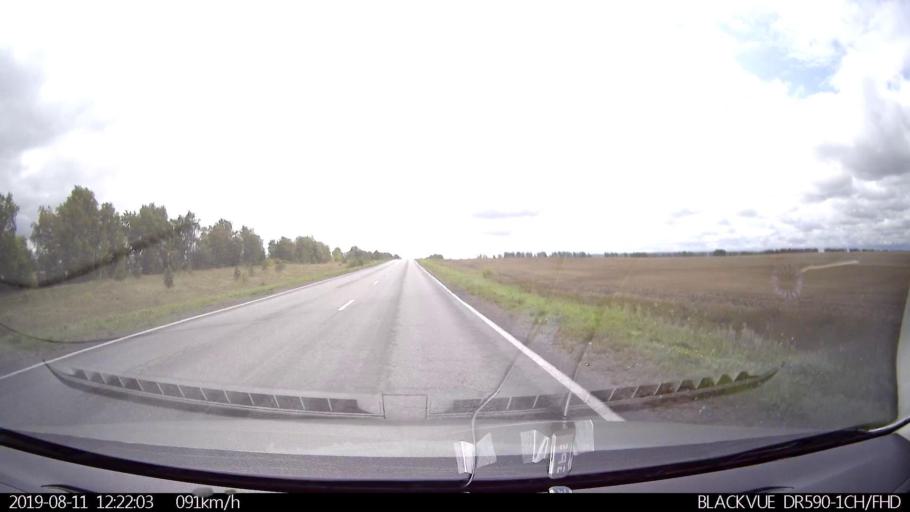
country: RU
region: Ulyanovsk
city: Ignatovka
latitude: 53.9137
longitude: 47.9558
